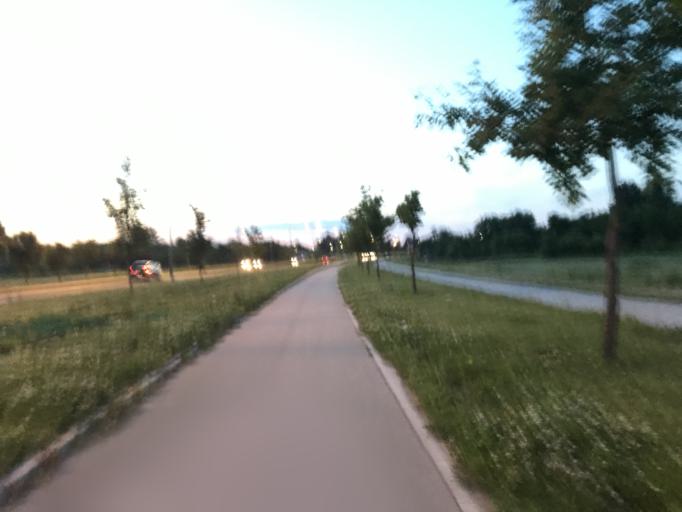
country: RS
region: Autonomna Pokrajina Vojvodina
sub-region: Juznobacki Okrug
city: Novi Sad
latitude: 45.2721
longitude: 19.8011
